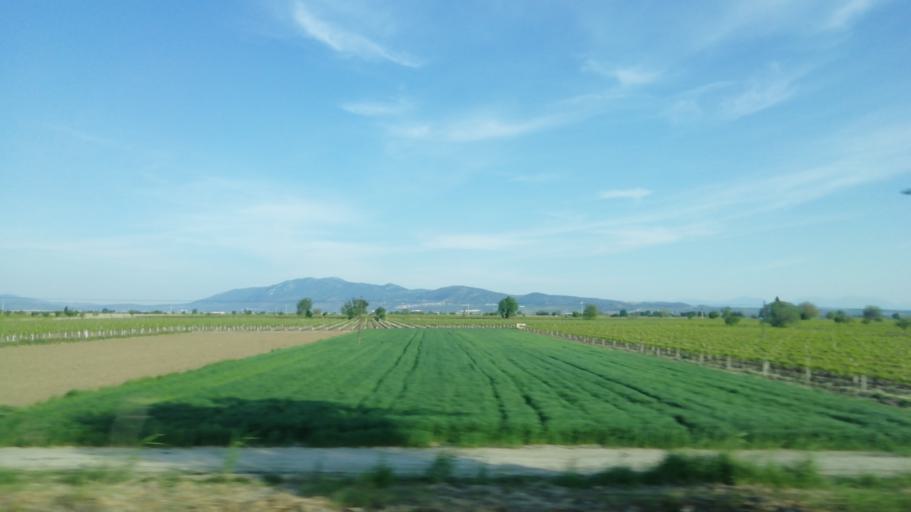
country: TR
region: Manisa
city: Saruhanli
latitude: 38.7500
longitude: 27.6216
